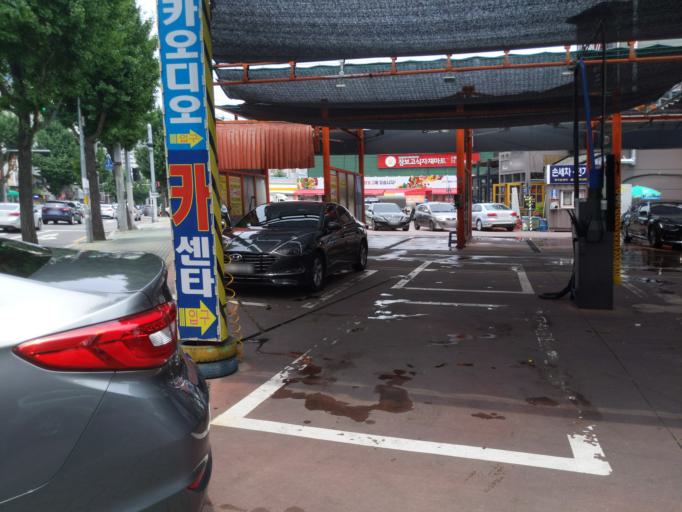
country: KR
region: Daegu
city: Hwawon
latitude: 35.8102
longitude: 128.5264
